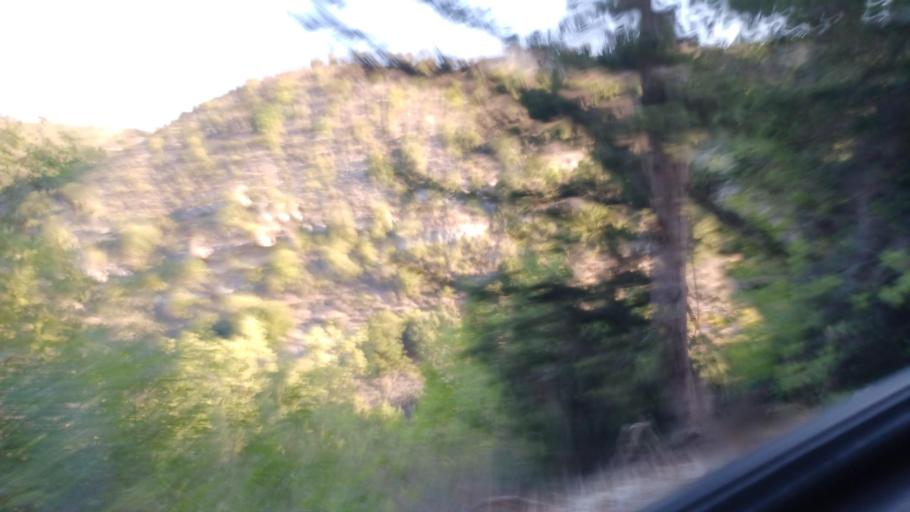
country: CY
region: Pafos
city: Tala
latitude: 34.8696
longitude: 32.4665
